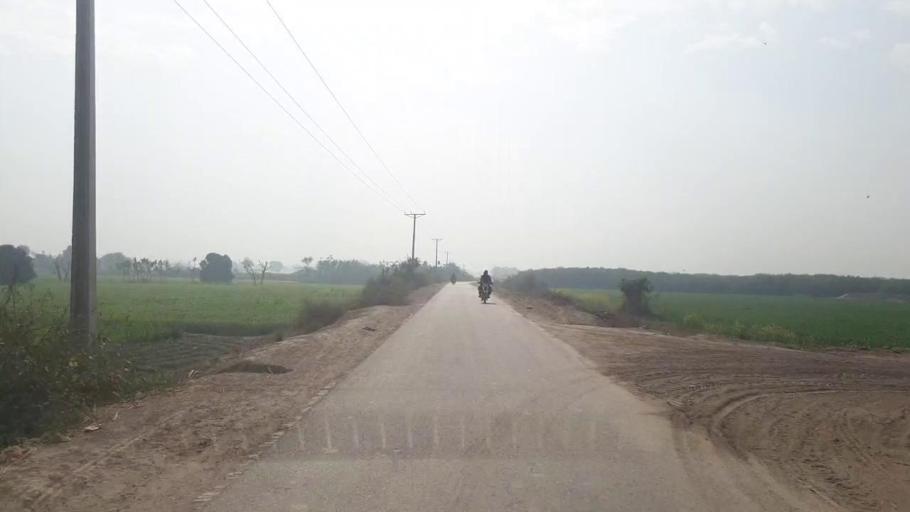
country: PK
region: Sindh
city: Hala
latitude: 25.7669
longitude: 68.4470
